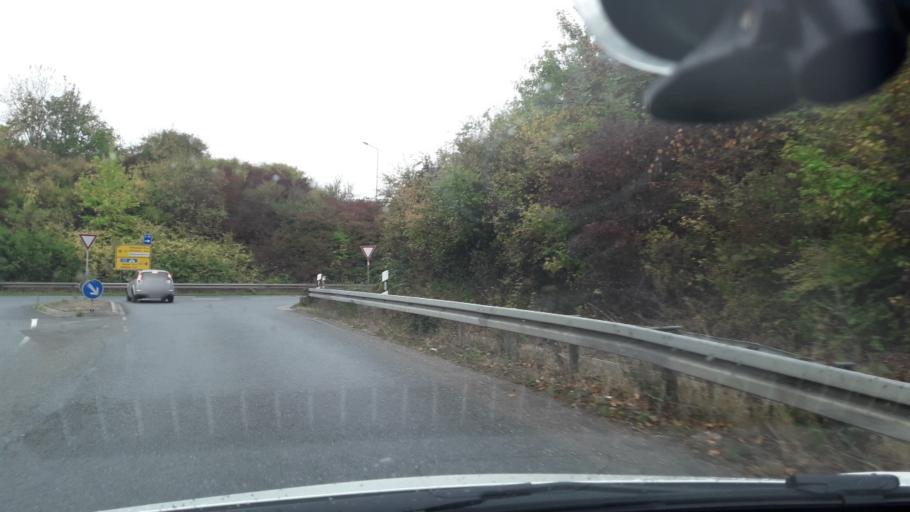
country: DE
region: Lower Saxony
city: Schladen
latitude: 52.0285
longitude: 10.5357
